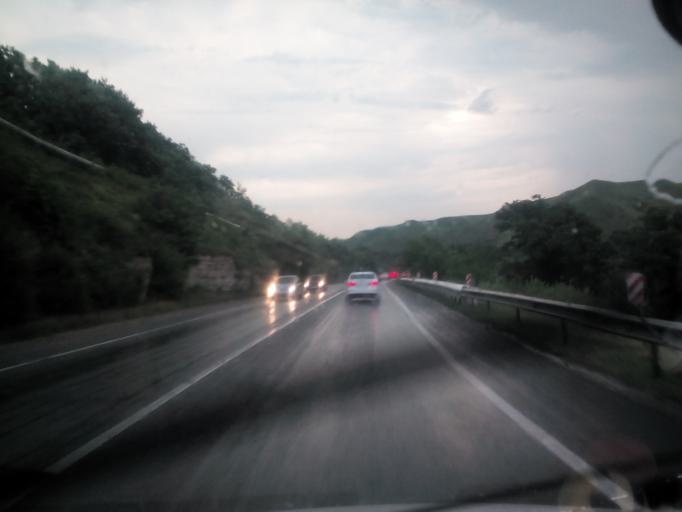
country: RU
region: Stavropol'skiy
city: Yasnaya Polyana
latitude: 43.9847
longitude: 42.7926
